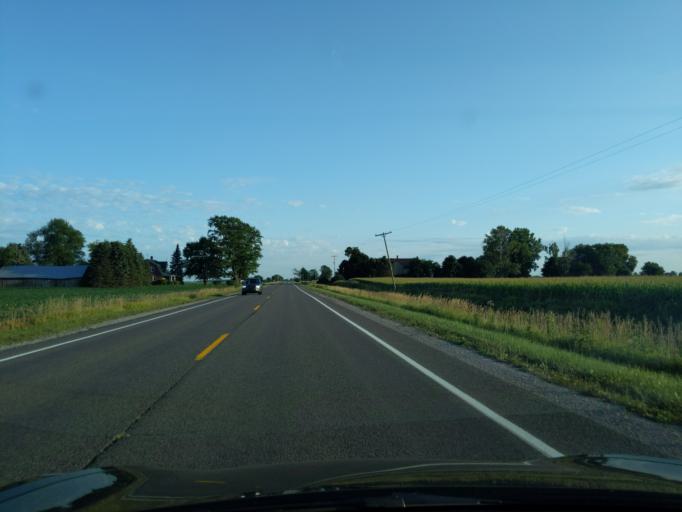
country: US
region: Michigan
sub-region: Gratiot County
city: Breckenridge
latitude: 43.5019
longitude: -84.3698
